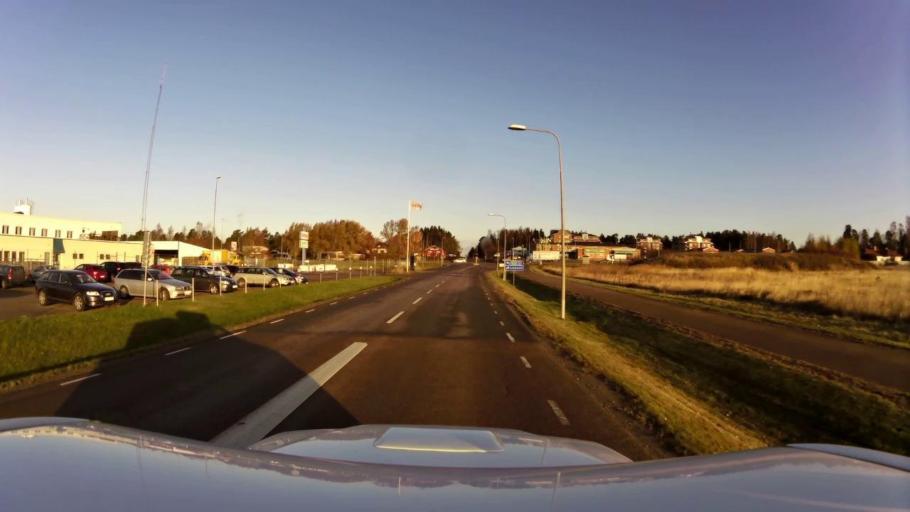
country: SE
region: OEstergoetland
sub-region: Linkopings Kommun
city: Linkoping
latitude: 58.4244
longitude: 15.6784
